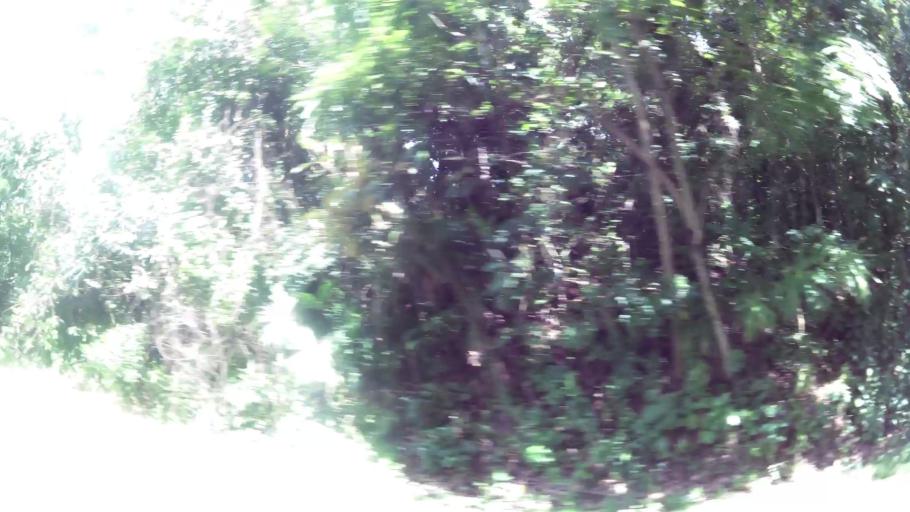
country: PA
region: Panama
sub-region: Distrito de Panama
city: Paraiso
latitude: 9.0338
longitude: -79.6246
